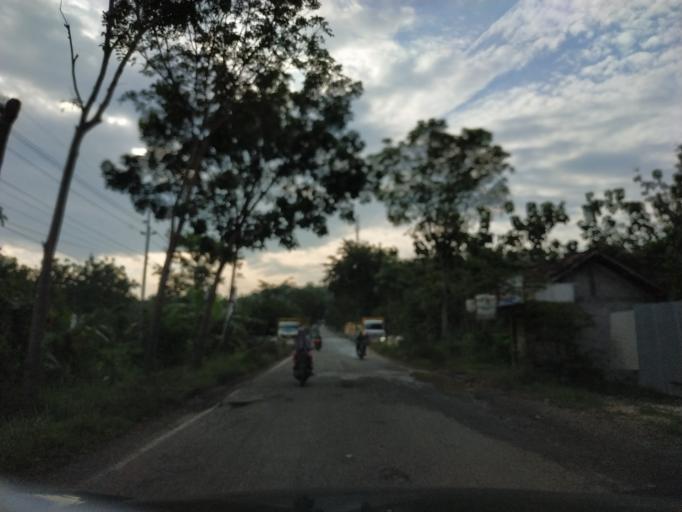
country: ID
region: Central Java
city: Ngampel
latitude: -6.9019
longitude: 111.4422
